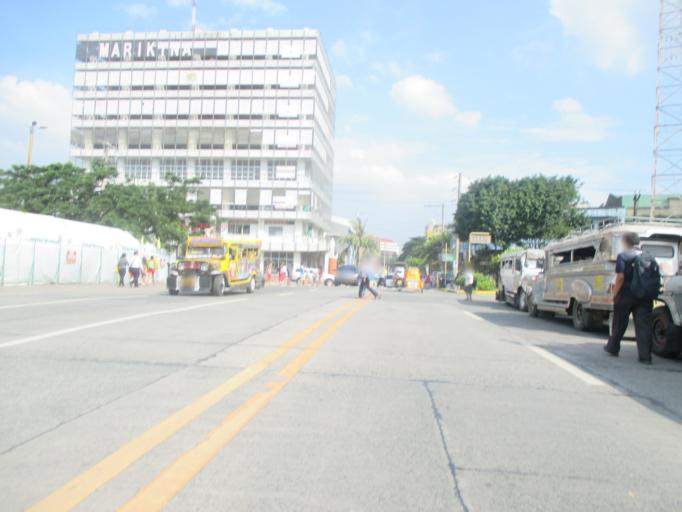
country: PH
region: Metro Manila
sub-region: Marikina
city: Calumpang
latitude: 14.6332
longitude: 121.0995
